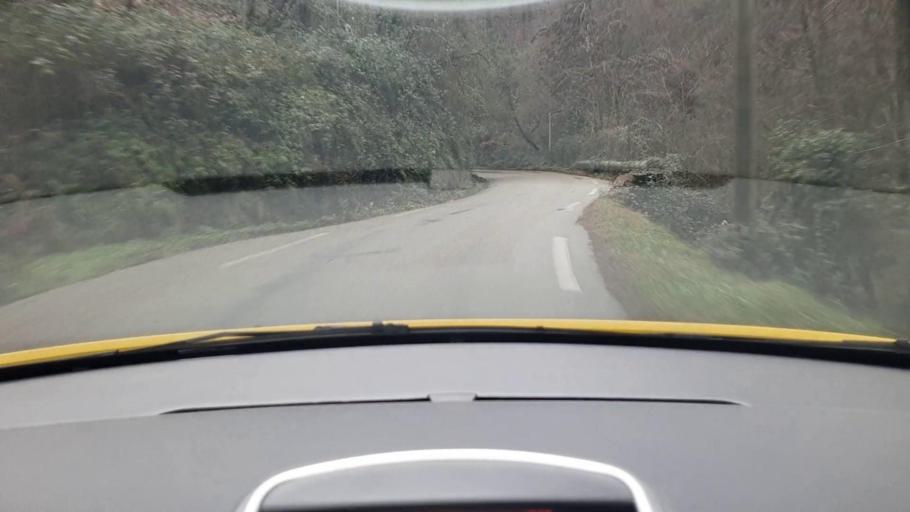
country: FR
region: Languedoc-Roussillon
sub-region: Departement du Gard
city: Besseges
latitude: 44.2772
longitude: 4.0726
